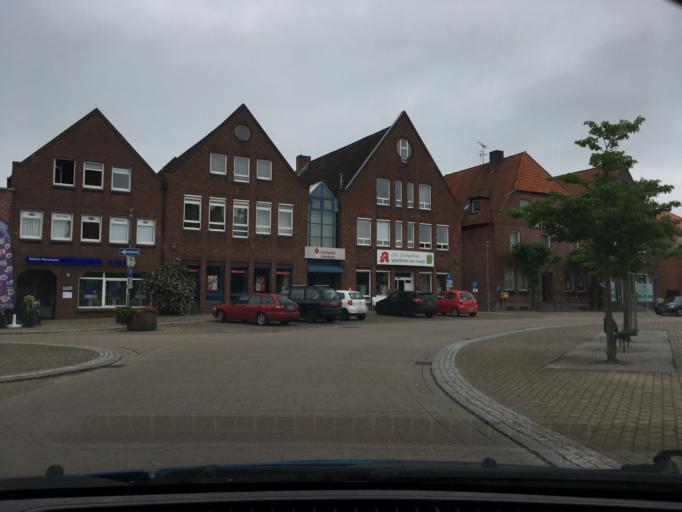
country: DE
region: Lower Saxony
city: Dahlenburg
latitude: 53.1869
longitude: 10.7425
